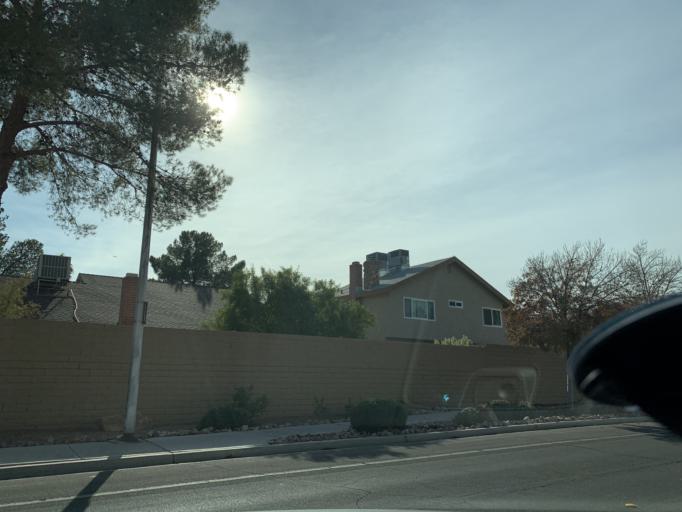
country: US
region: Nevada
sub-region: Clark County
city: Spring Valley
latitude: 36.1072
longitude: -115.2366
